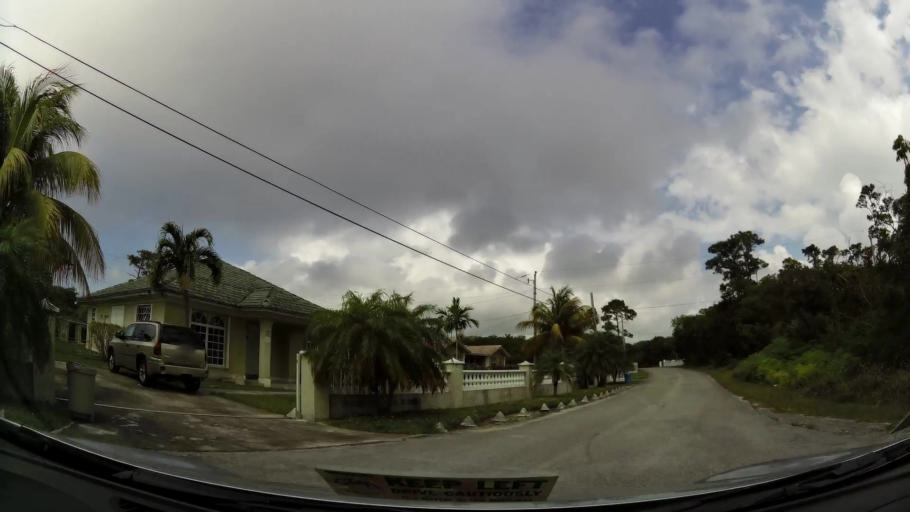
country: BS
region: Freeport
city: Lucaya
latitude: 26.5402
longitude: -78.5961
